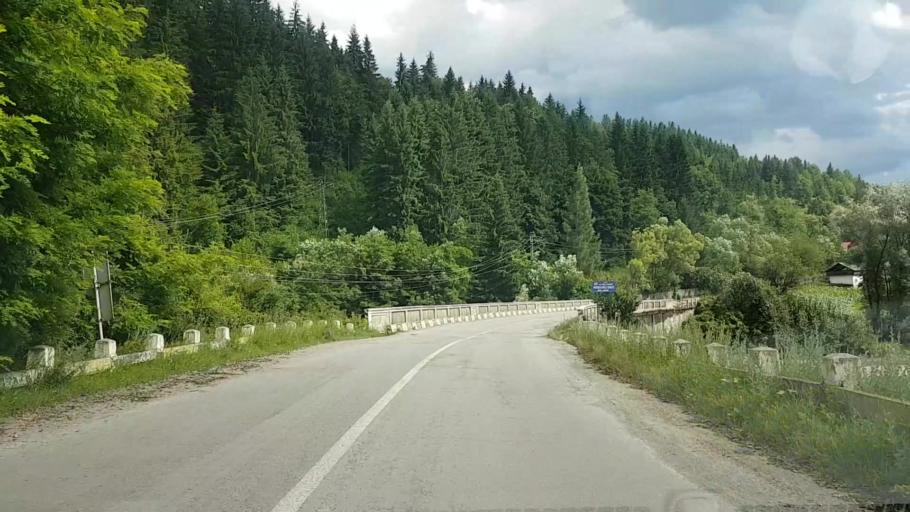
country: RO
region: Neamt
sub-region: Comuna Hangu
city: Hangu
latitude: 47.0593
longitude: 26.0364
